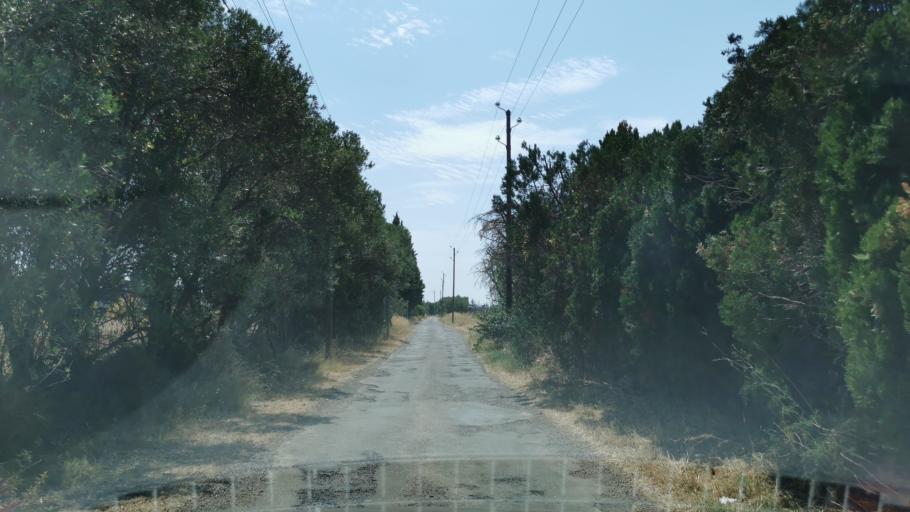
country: FR
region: Languedoc-Roussillon
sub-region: Departement de l'Aude
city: Bize-Minervois
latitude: 43.2942
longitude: 2.8831
